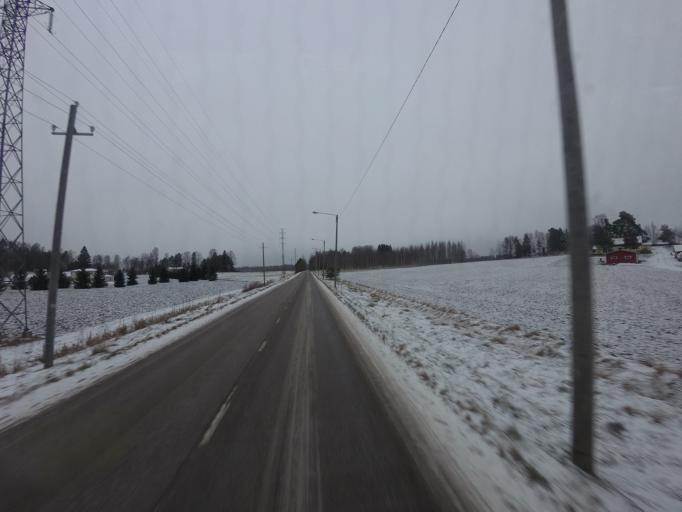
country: FI
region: Uusimaa
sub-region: Helsinki
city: Espoo
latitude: 60.1941
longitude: 24.5702
